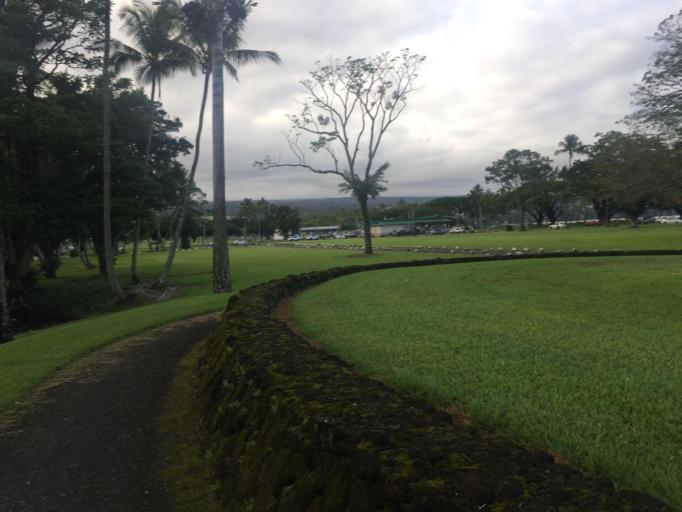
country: US
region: Hawaii
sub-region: Hawaii County
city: Hilo
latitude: 19.7207
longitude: -155.0769
